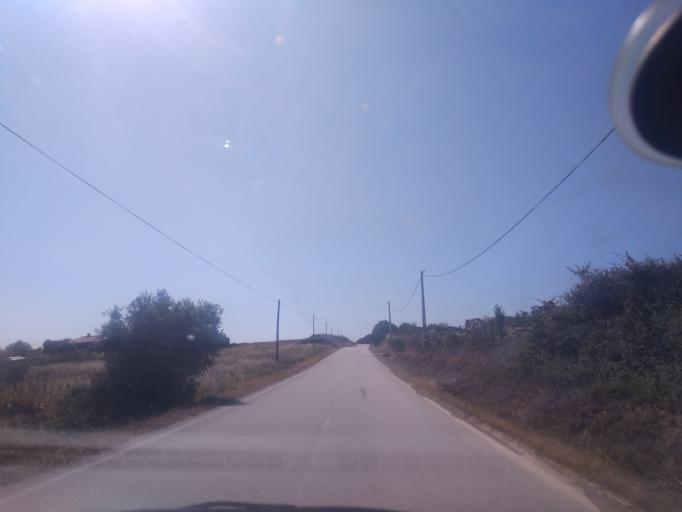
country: PT
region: Faro
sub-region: Aljezur
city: Aljezur
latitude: 37.2242
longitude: -8.8092
